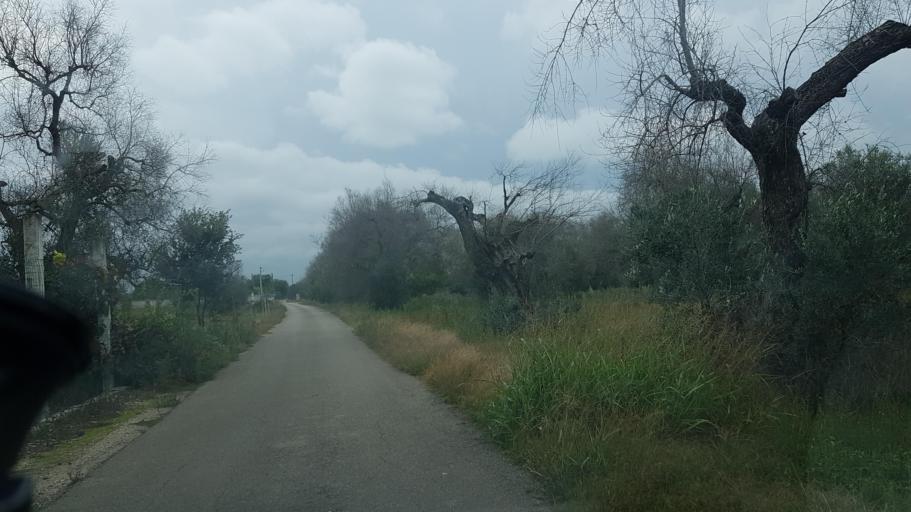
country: IT
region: Apulia
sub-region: Provincia di Brindisi
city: San Donaci
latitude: 40.4529
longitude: 17.9354
